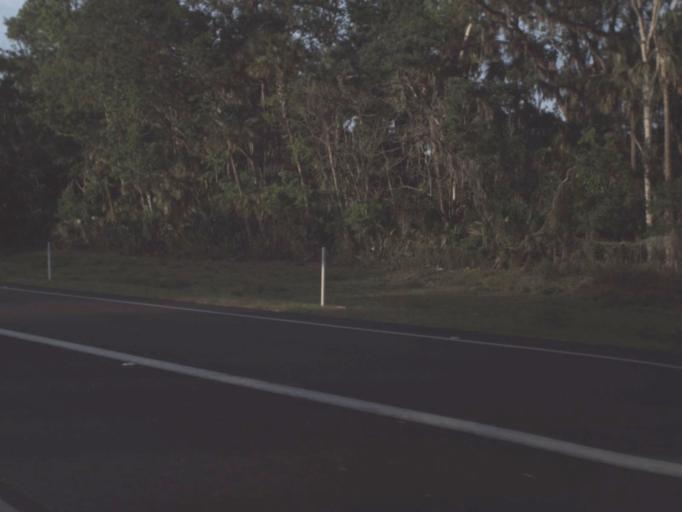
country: US
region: Florida
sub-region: Brevard County
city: Mims
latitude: 28.6703
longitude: -80.8713
